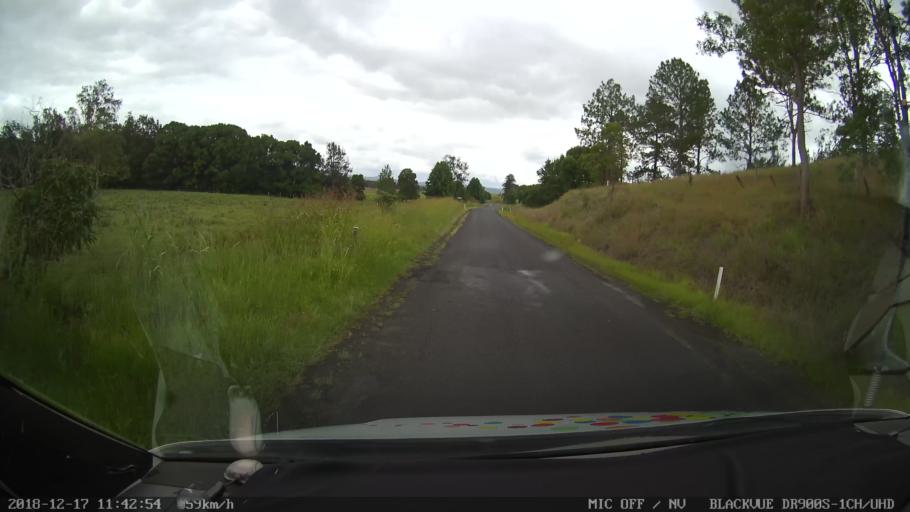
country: AU
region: New South Wales
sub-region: Kyogle
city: Kyogle
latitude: -28.6647
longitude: 152.5926
